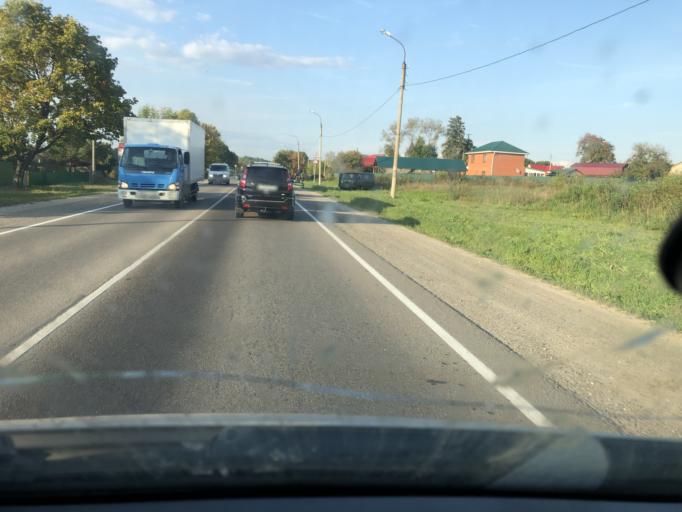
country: RU
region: Kaluga
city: Peremyshl'
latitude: 54.3782
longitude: 36.1980
